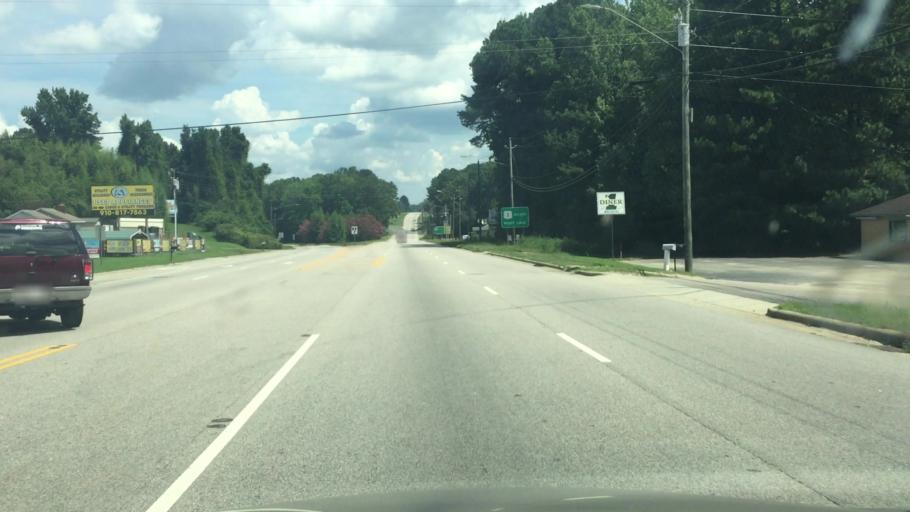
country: US
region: North Carolina
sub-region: Richmond County
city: Rockingham
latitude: 34.9209
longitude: -79.7829
